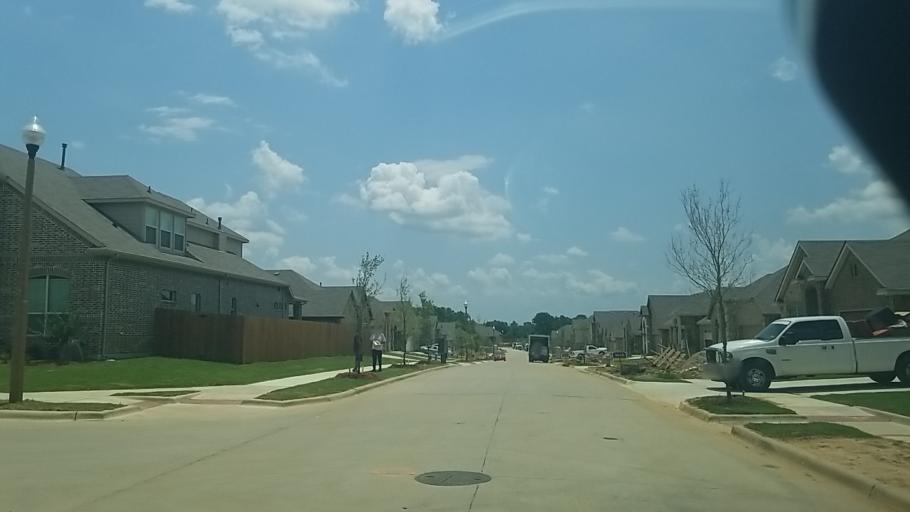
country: US
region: Texas
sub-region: Denton County
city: Denton
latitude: 33.1713
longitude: -97.1170
